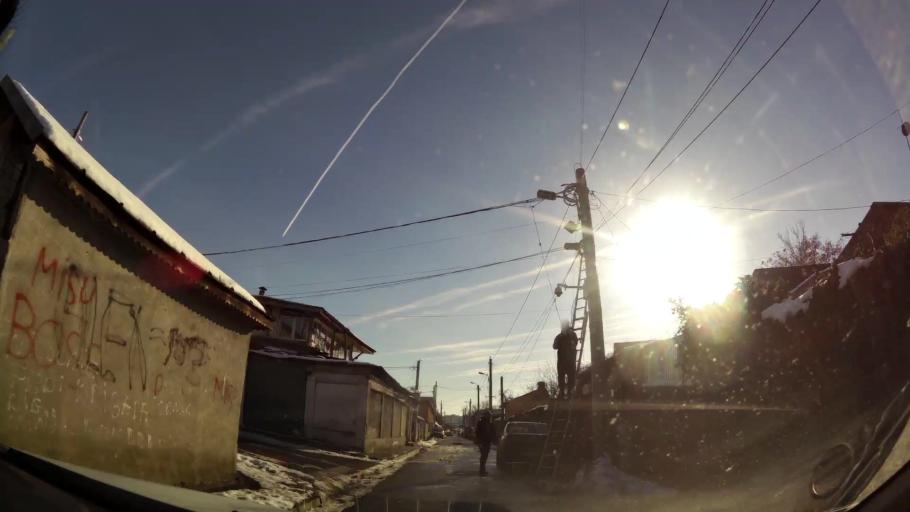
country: RO
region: Ilfov
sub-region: Comuna Fundeni-Dobroesti
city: Fundeni
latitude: 44.4730
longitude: 26.1292
